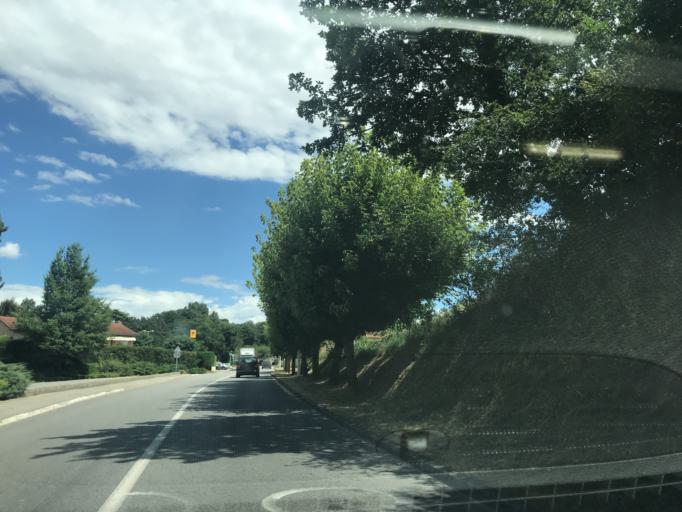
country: FR
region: Rhone-Alpes
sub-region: Departement de la Drome
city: Chateauneuf-sur-Isere
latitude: 45.0150
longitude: 4.9461
